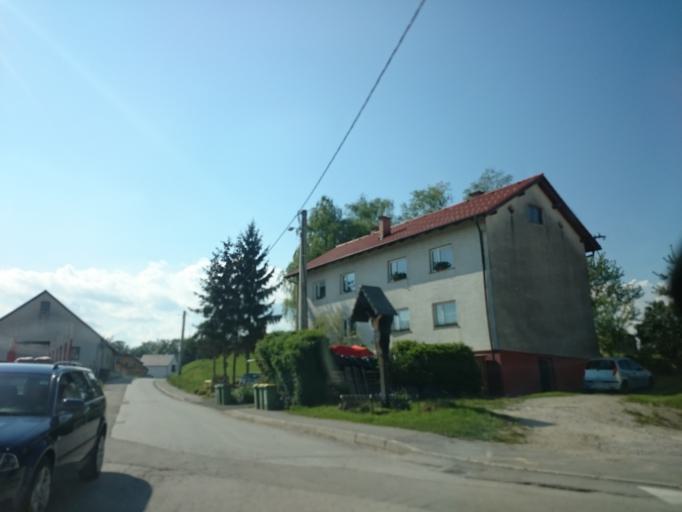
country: SI
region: Sentjur pri Celju
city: Sentjur
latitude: 46.2727
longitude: 15.3912
